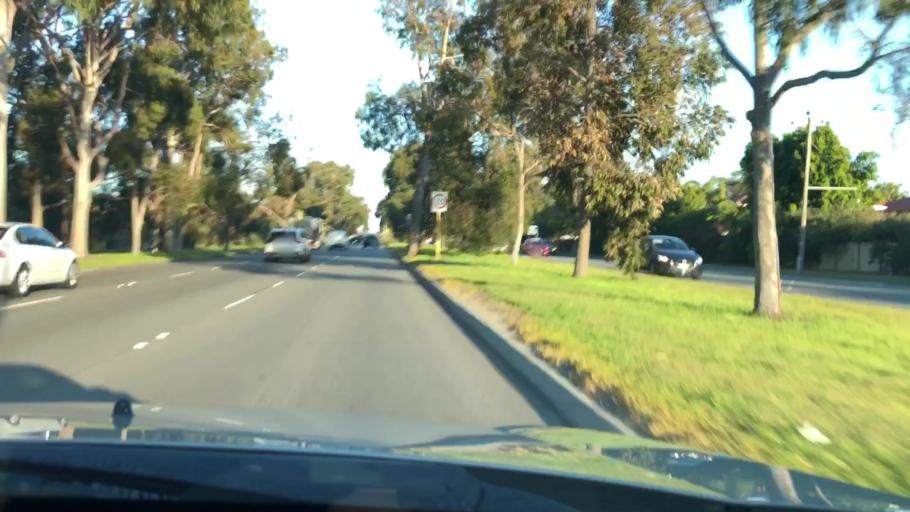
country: AU
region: Western Australia
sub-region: Melville
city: Booragoon
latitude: -32.0461
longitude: 115.8352
